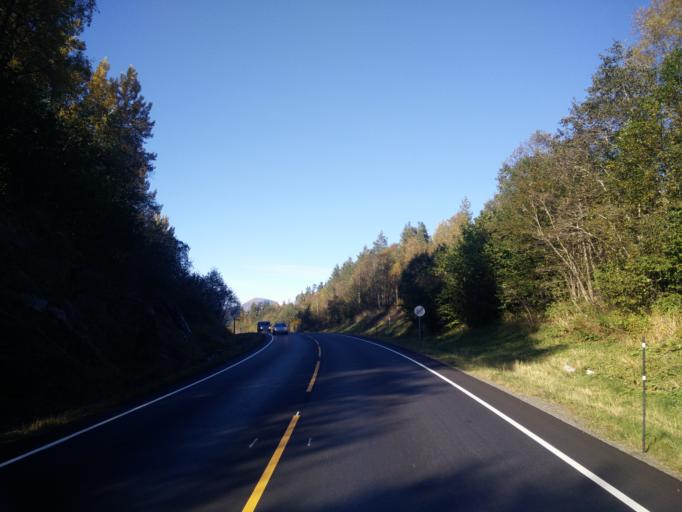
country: NO
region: More og Romsdal
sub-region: Halsa
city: Liaboen
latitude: 63.0908
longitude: 8.3518
